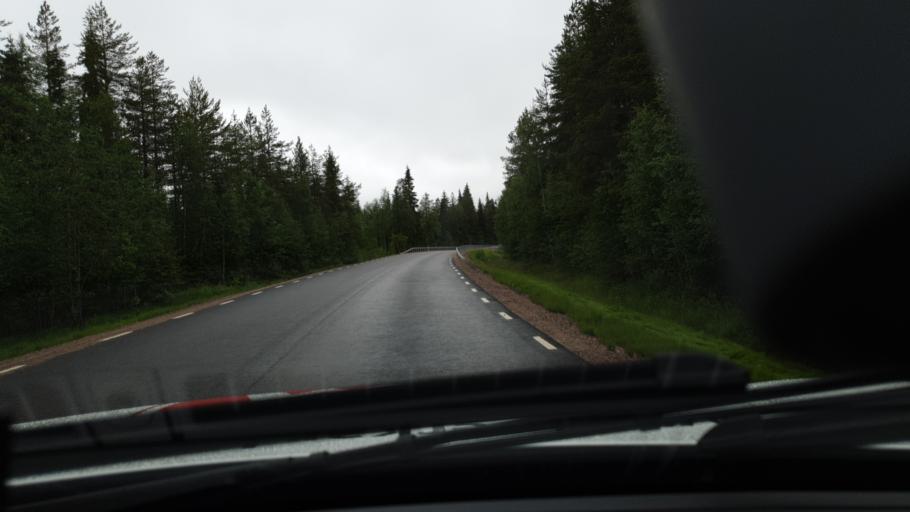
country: SE
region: Norrbotten
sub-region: Overtornea Kommun
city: OEvertornea
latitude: 66.4211
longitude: 23.5512
